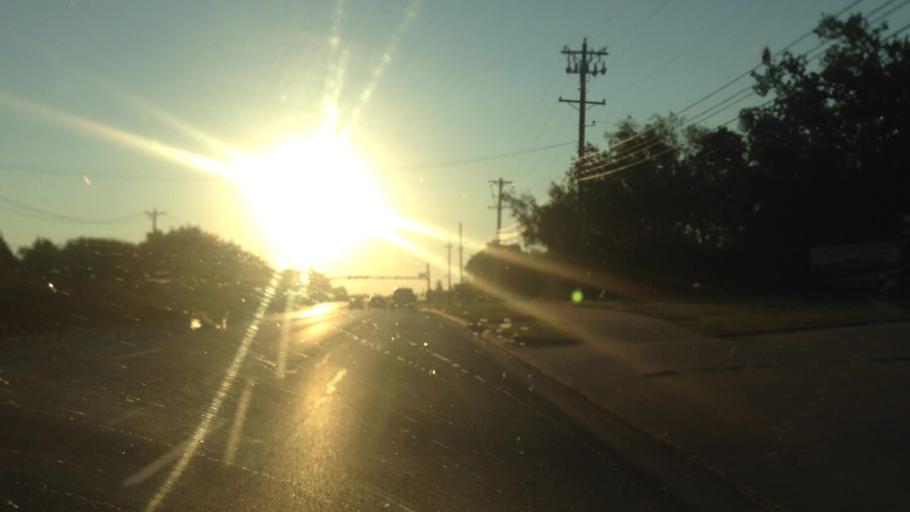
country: US
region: Texas
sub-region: Tarrant County
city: Southlake
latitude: 32.9410
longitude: -97.1392
